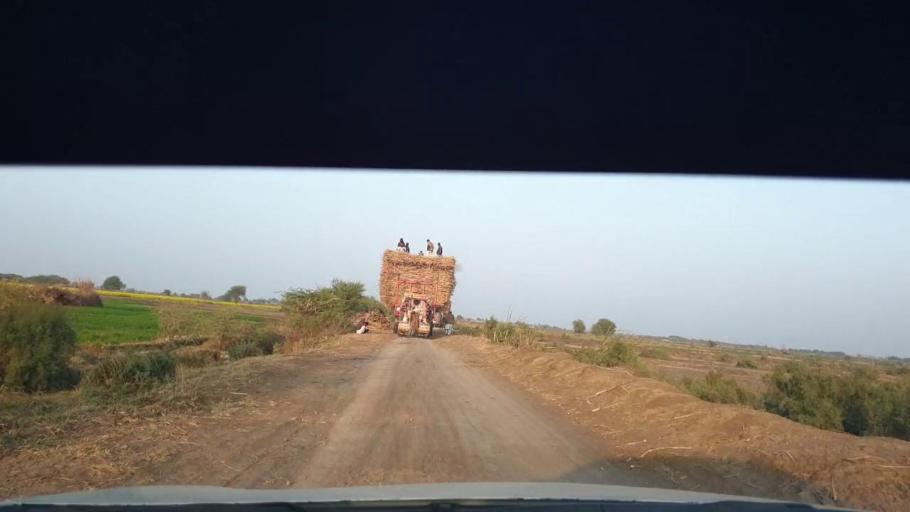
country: PK
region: Sindh
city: Berani
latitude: 25.7454
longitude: 68.9726
